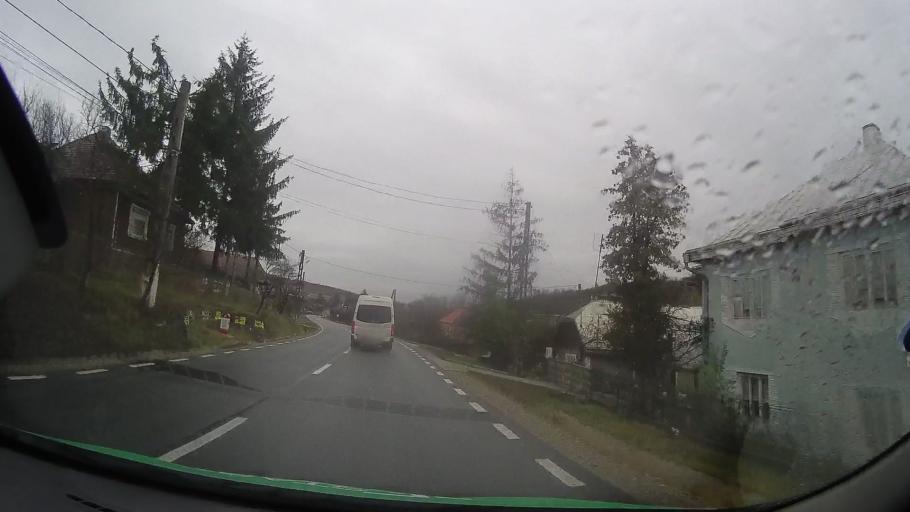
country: RO
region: Bistrita-Nasaud
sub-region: Comuna Galatii Bistritei
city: Galatii Bistritei
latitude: 47.0248
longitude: 24.4155
